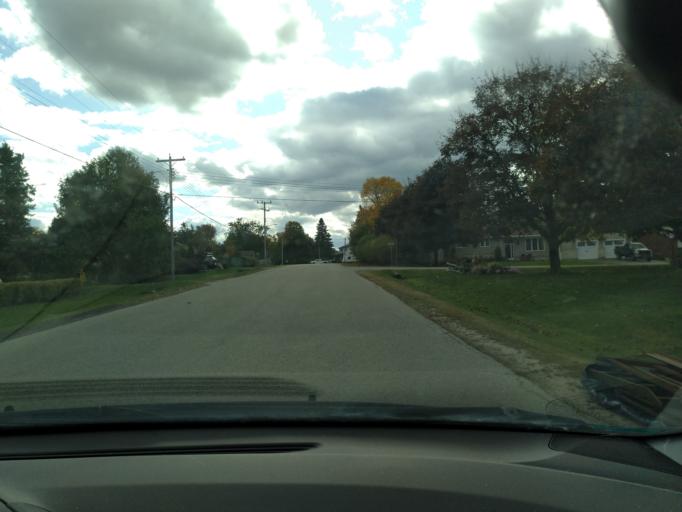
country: CA
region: Ontario
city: Bradford West Gwillimbury
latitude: 44.0879
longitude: -79.6807
